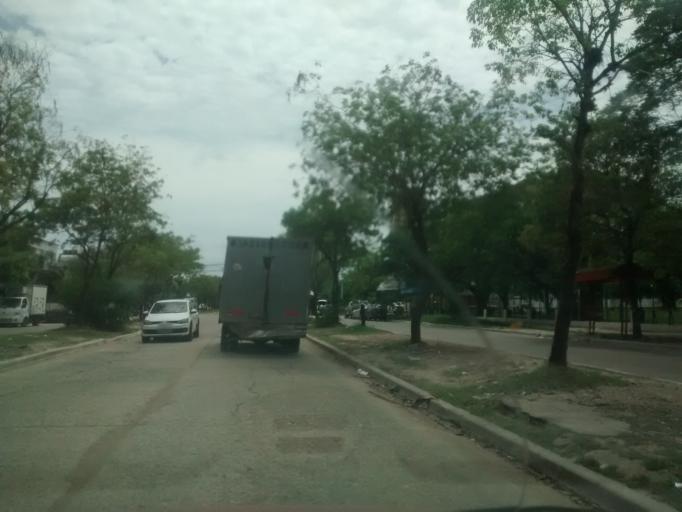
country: AR
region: Chaco
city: Resistencia
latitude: -27.4626
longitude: -58.9851
